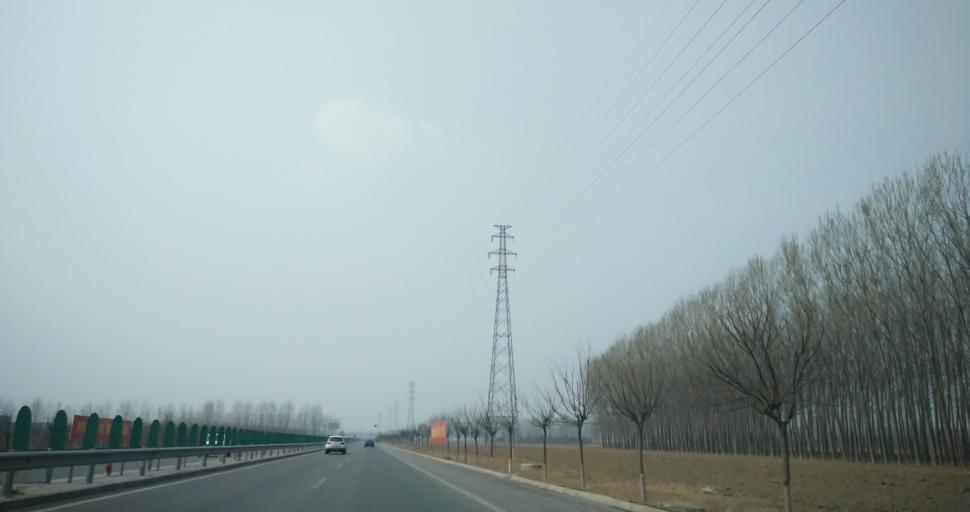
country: CN
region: Beijing
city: Qingyundian
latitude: 39.6935
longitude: 116.4841
